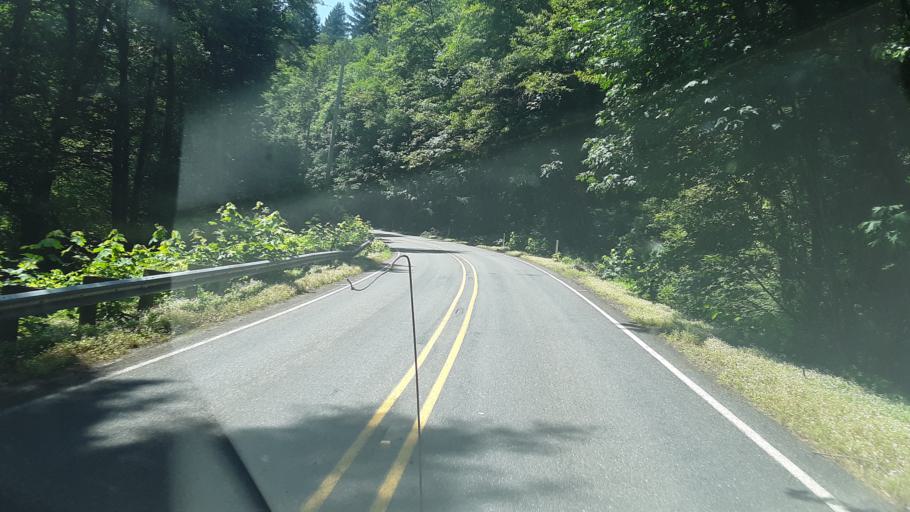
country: US
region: Washington
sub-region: Clark County
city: Amboy
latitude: 46.0154
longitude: -122.3307
